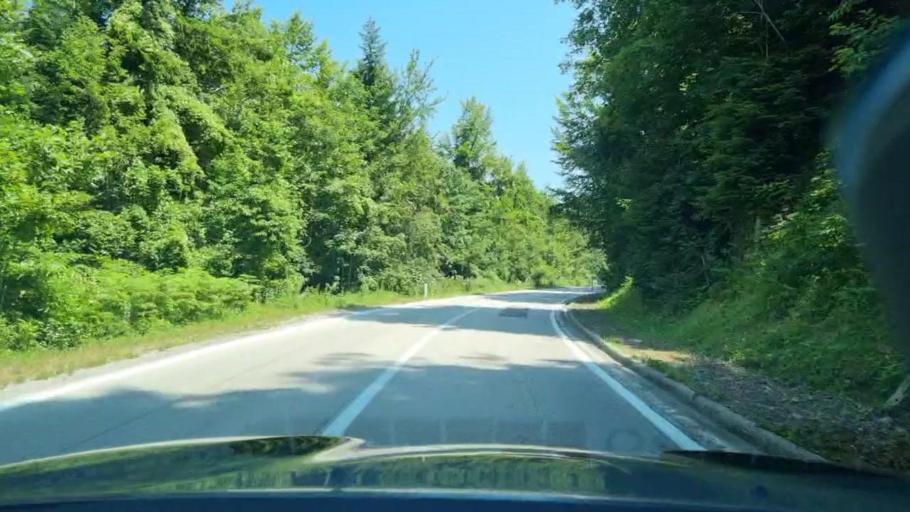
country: BA
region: Federation of Bosnia and Herzegovina
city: Sanica
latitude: 44.4926
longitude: 16.3858
